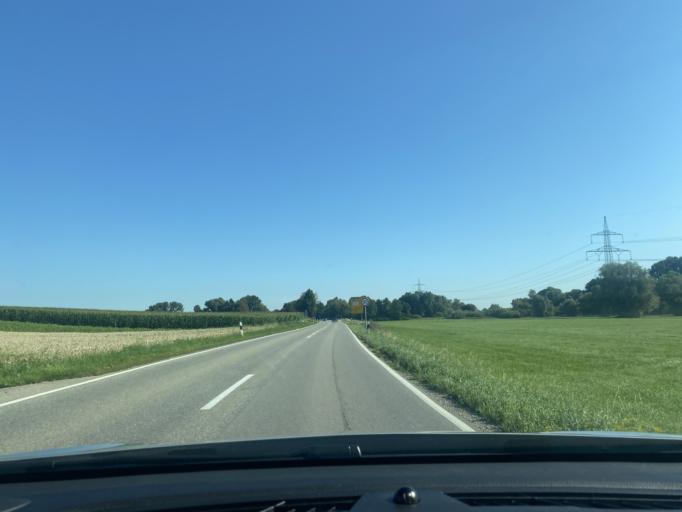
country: DE
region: Bavaria
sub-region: Upper Bavaria
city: Eitting
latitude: 48.3489
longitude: 11.8975
